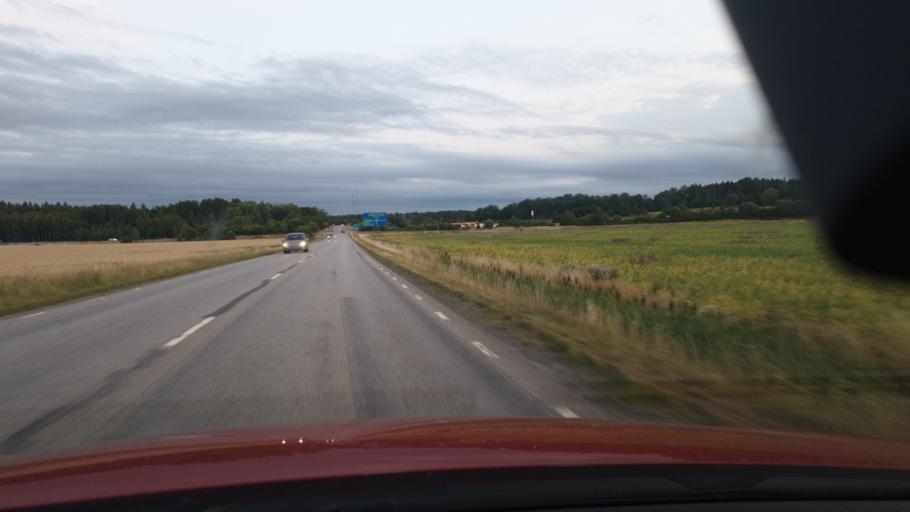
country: SE
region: Uppsala
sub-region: Habo Kommun
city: Balsta
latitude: 59.5910
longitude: 17.5101
